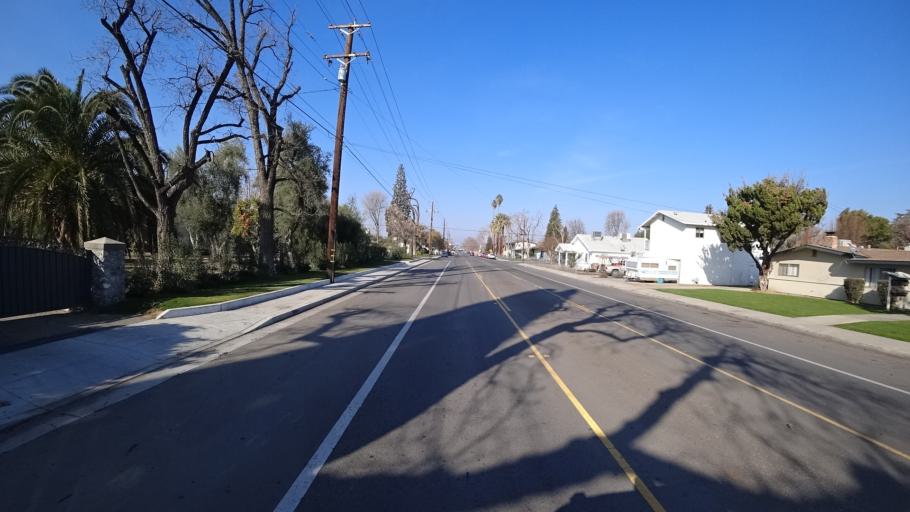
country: US
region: California
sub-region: Kern County
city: Bakersfield
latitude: 35.3624
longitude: -119.0295
